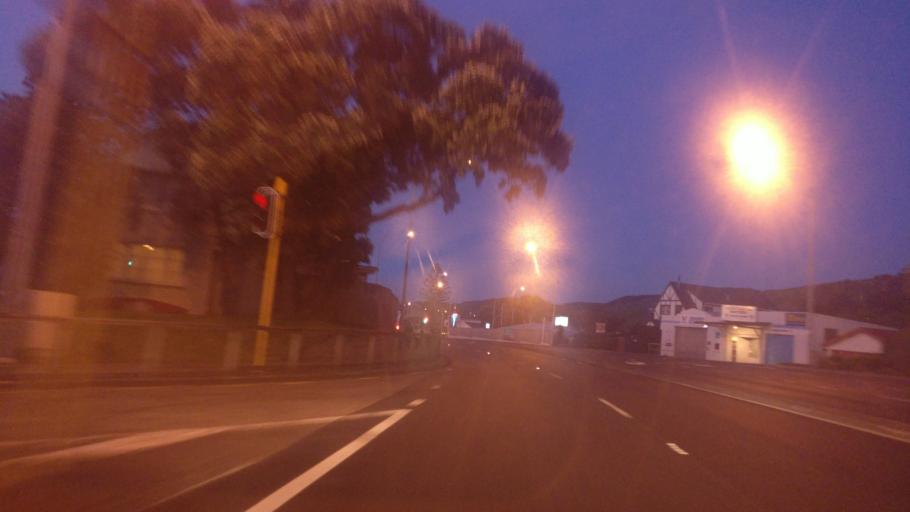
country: NZ
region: Wellington
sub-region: Porirua City
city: Porirua
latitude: -41.0868
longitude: 174.8682
